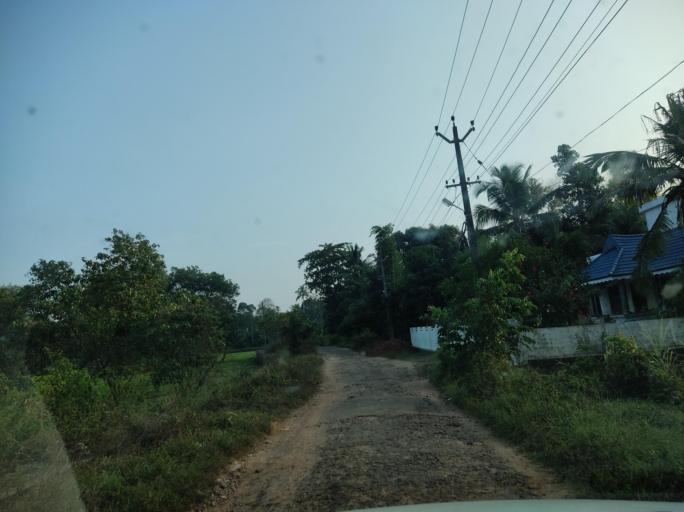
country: IN
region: Kerala
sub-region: Pattanamtitta
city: Tiruvalla
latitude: 9.3627
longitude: 76.5647
